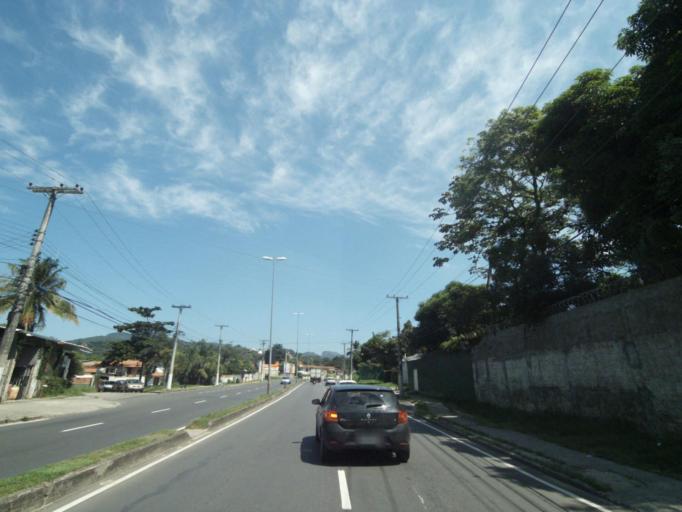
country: BR
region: Rio de Janeiro
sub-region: Sao Goncalo
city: Sao Goncalo
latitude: -22.8797
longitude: -43.0273
